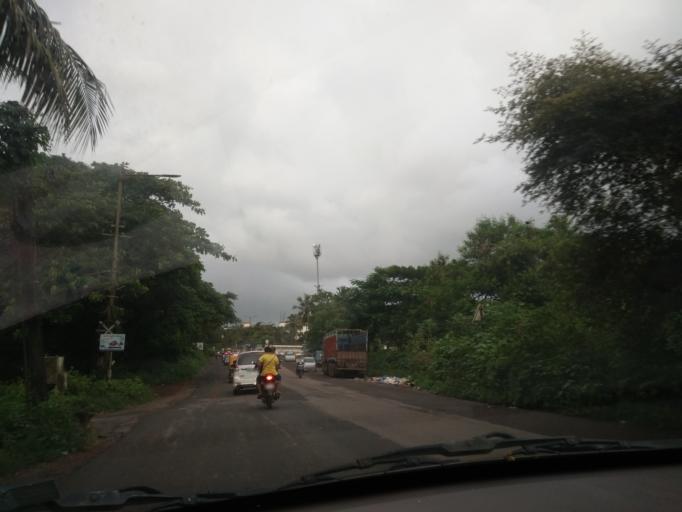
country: IN
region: Goa
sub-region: South Goa
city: Davorlim
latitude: 15.2662
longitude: 73.9778
